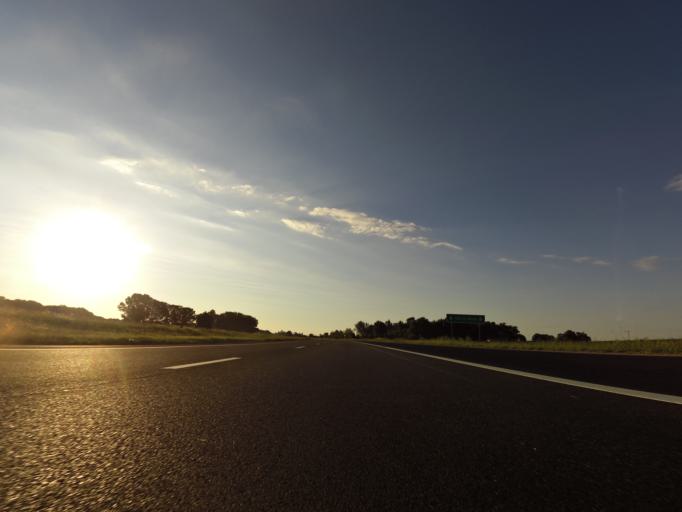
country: US
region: Kansas
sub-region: Sedgwick County
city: Colwich
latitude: 37.8279
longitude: -97.5576
